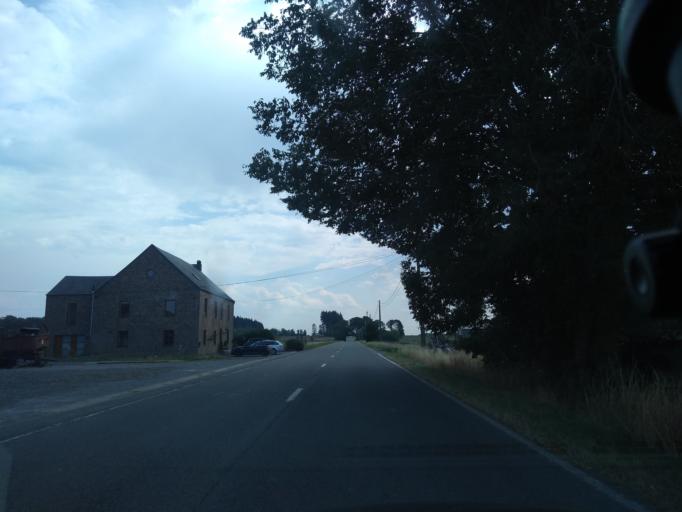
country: BE
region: Wallonia
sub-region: Province de Namur
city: Dinant
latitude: 50.1856
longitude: 4.8999
